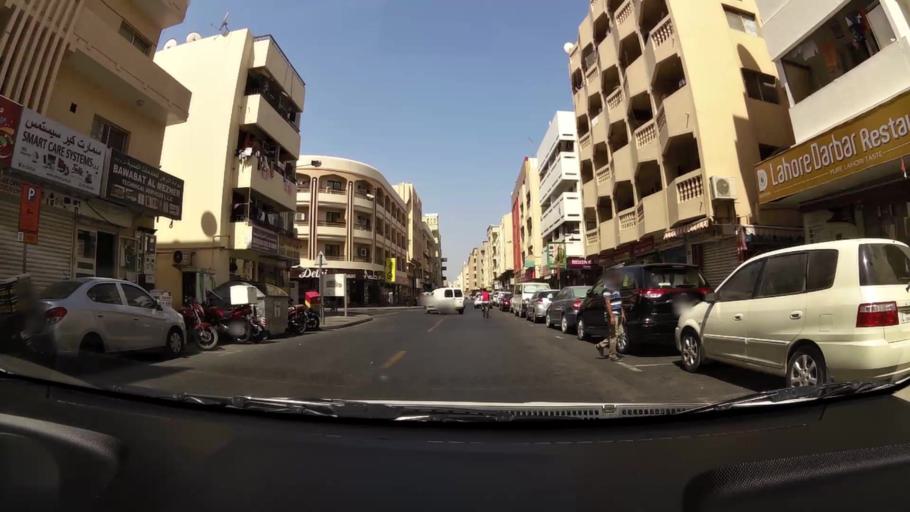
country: AE
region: Ash Shariqah
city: Sharjah
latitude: 25.2763
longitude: 55.3120
